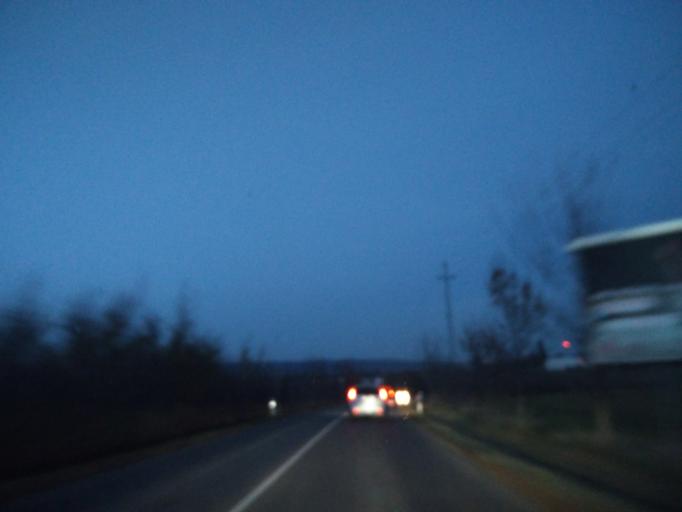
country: HU
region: Pest
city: Budakeszi
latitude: 47.4853
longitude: 18.9057
